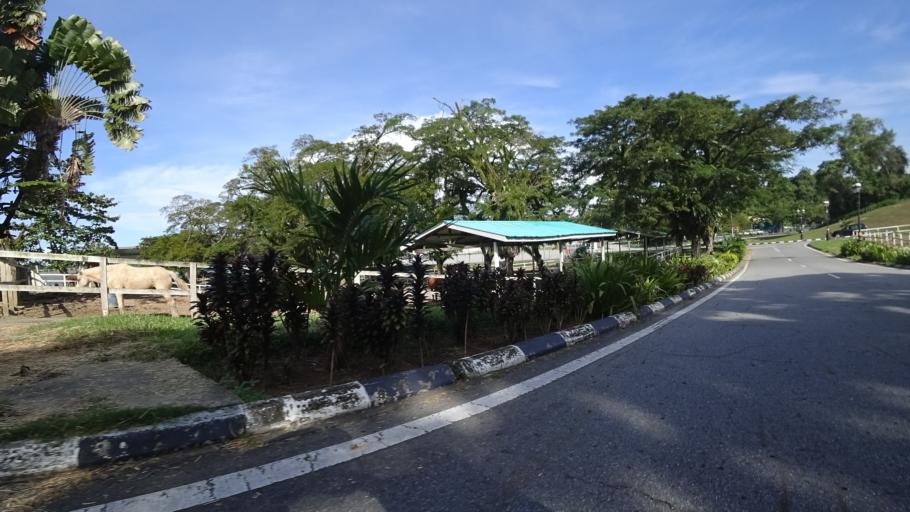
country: BN
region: Brunei and Muara
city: Bandar Seri Begawan
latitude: 4.9485
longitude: 114.8335
